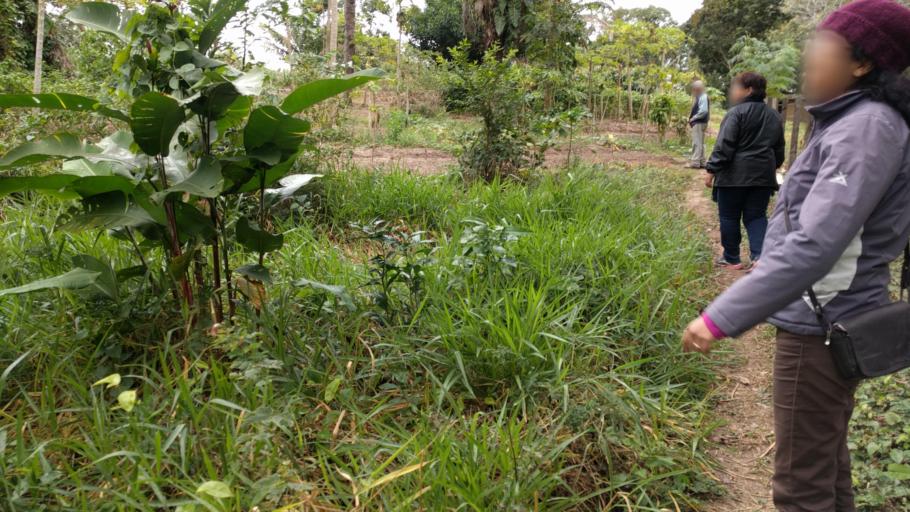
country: BO
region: Santa Cruz
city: San Juan del Surutu
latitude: -17.4593
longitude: -63.6965
